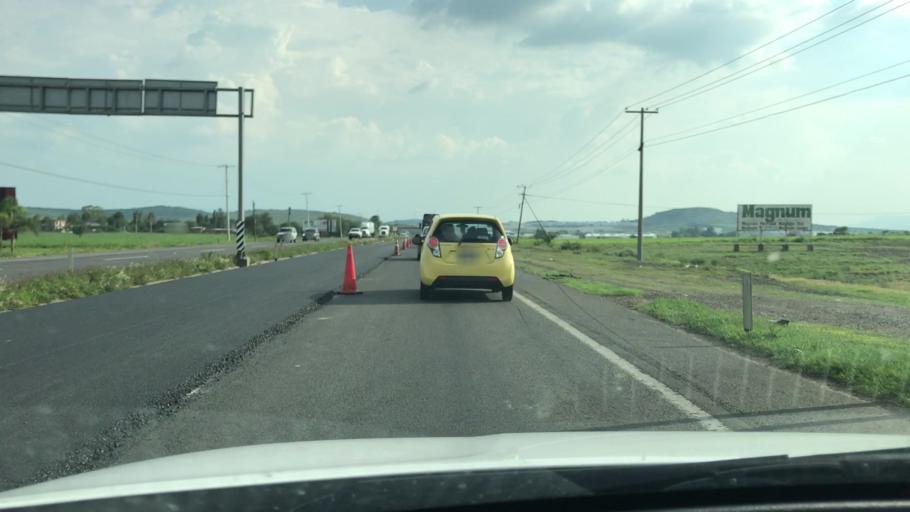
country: MX
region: Guanajuato
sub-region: Irapuato
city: Colonia Morelos de Guadalupe de Rivera
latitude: 20.5861
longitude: -101.4295
